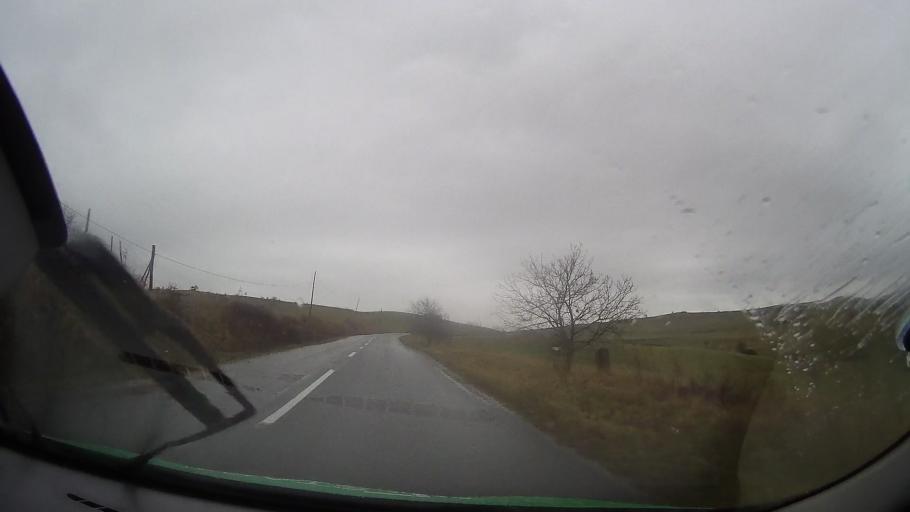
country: RO
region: Bistrita-Nasaud
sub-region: Comuna Monor
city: Monor
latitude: 46.9558
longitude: 24.6753
